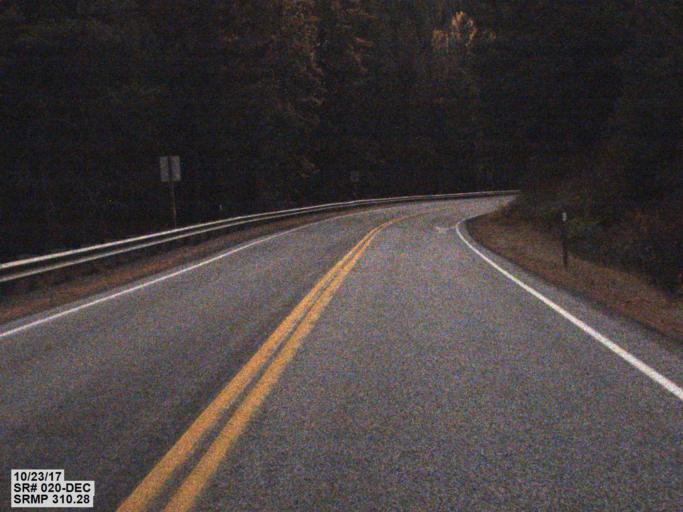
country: US
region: Washington
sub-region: Ferry County
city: Republic
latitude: 48.5964
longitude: -118.6304
